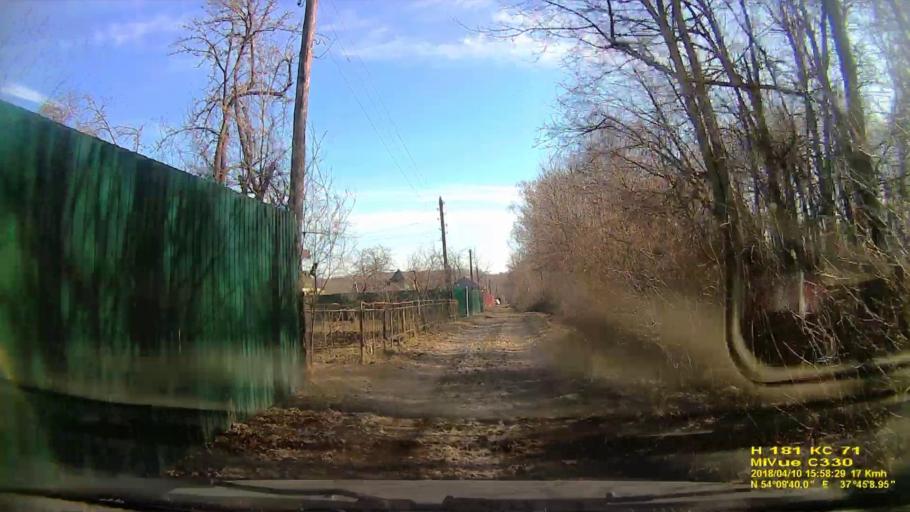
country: RU
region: Tula
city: Bolokhovo
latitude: 54.1611
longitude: 37.7525
